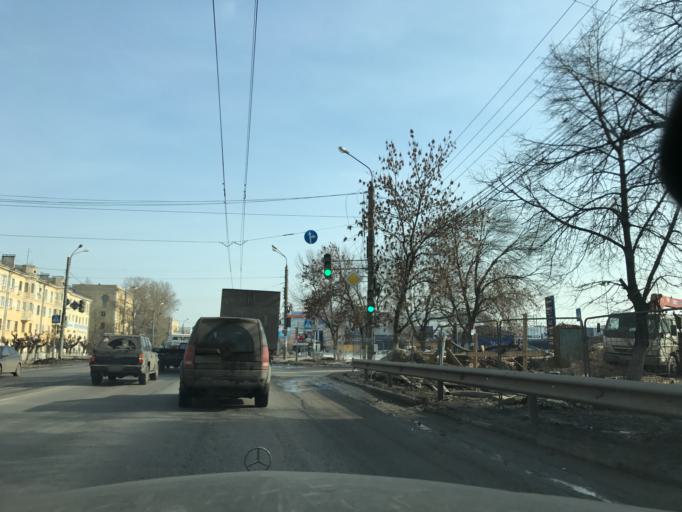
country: RU
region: Nizjnij Novgorod
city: Nizhniy Novgorod
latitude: 56.3175
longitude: 43.9186
